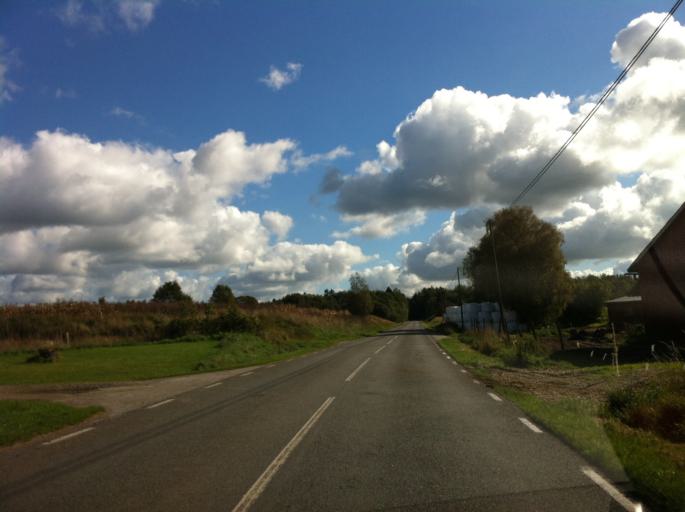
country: SE
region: Skane
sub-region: Kristianstads Kommun
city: Degeberga
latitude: 55.7750
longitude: 13.8942
